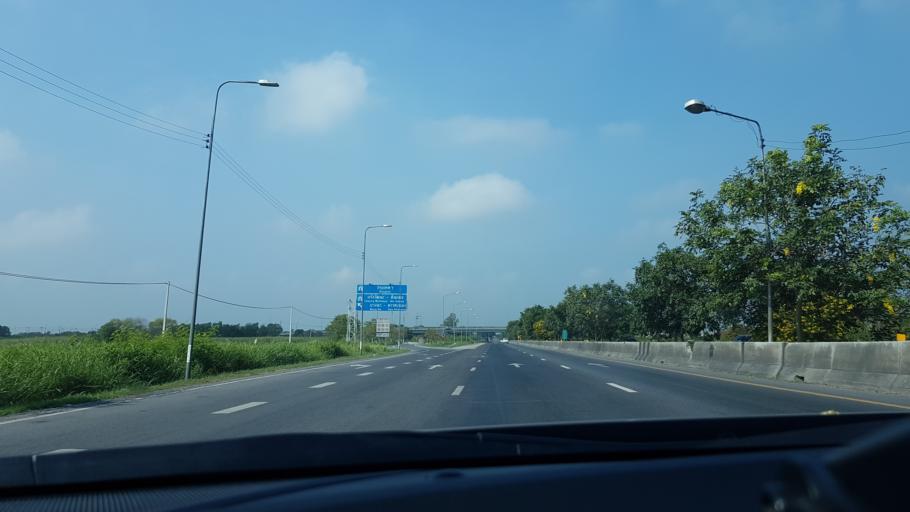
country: TH
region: Phra Nakhon Si Ayutthaya
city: Bang Pa-in
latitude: 14.1509
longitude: 100.5579
